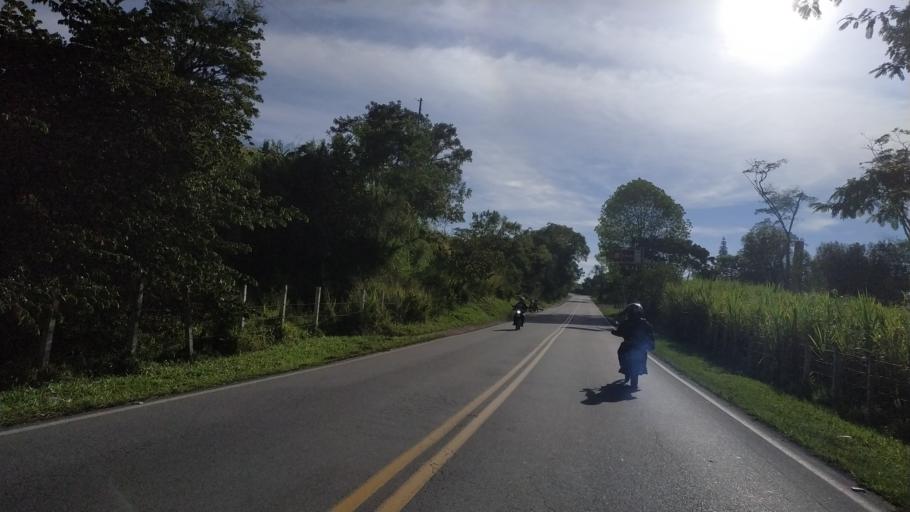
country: CO
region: Santander
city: Guepsa
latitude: 6.0164
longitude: -73.5801
